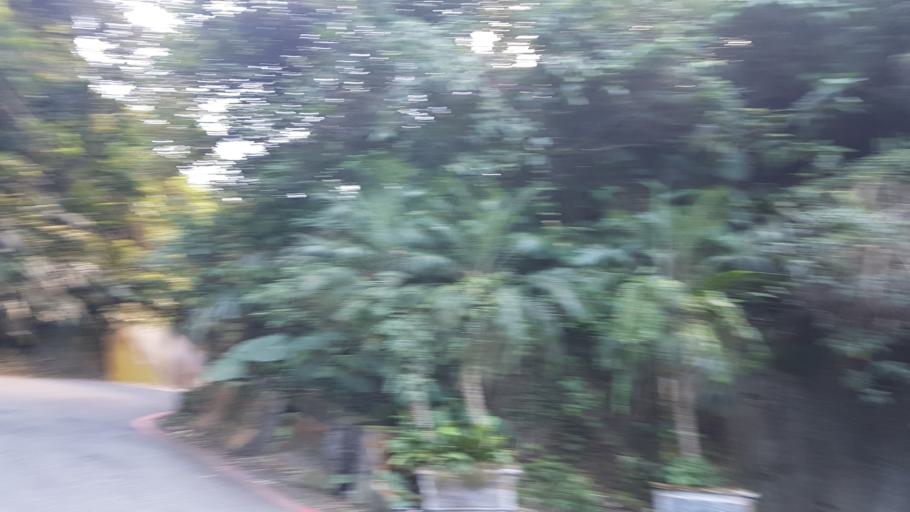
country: TW
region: Taipei
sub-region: Taipei
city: Banqiao
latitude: 24.9534
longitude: 121.5318
